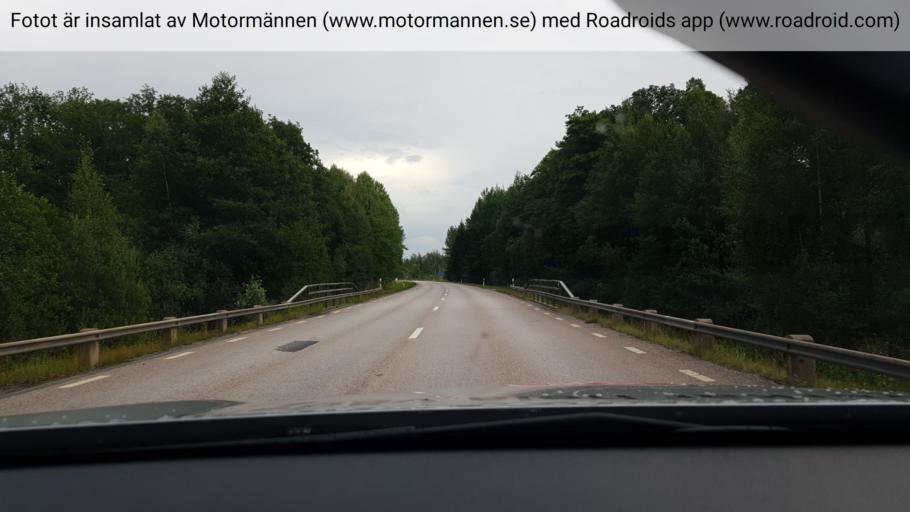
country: SE
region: Uppsala
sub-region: Osthammars Kommun
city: Osterbybruk
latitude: 60.4051
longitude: 17.8750
